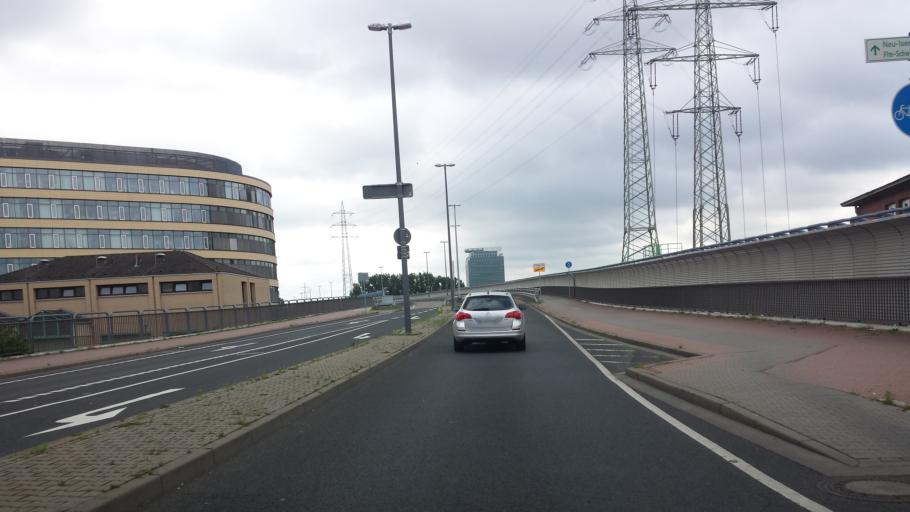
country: DE
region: Hesse
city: Kelsterbach
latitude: 50.0970
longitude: 8.5423
